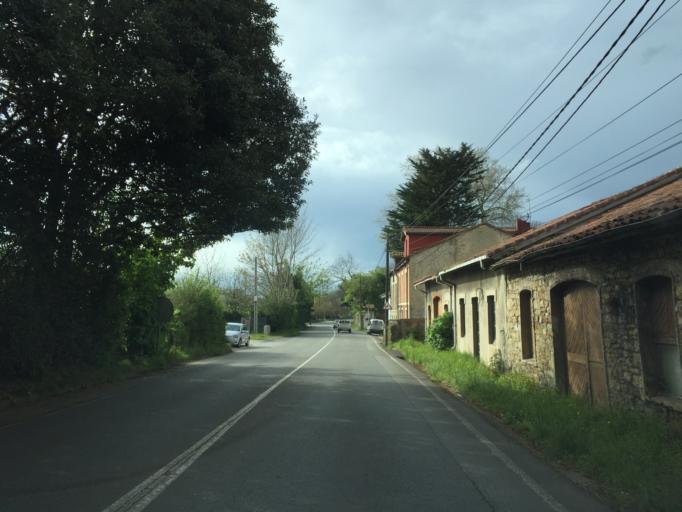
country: ES
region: Asturias
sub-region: Province of Asturias
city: Gijon
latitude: 43.5165
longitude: -5.6045
